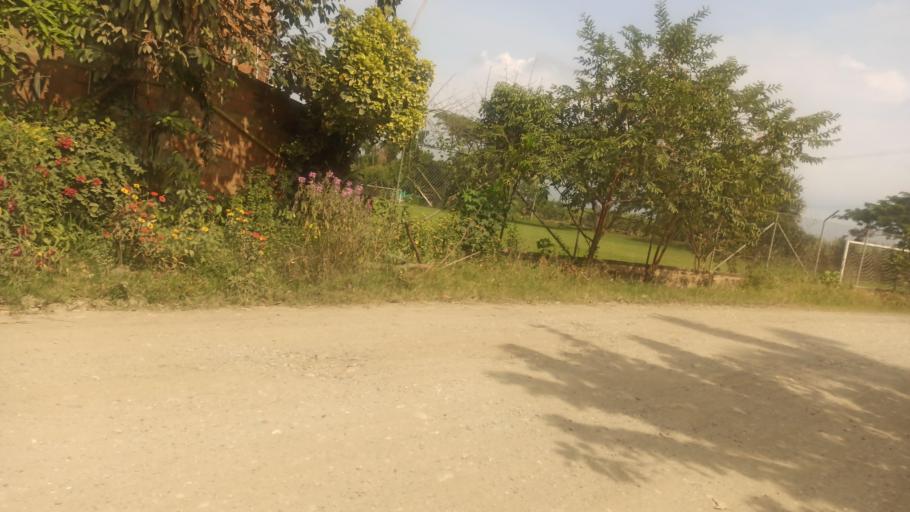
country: CO
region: Valle del Cauca
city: Jamundi
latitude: 3.2003
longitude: -76.5017
